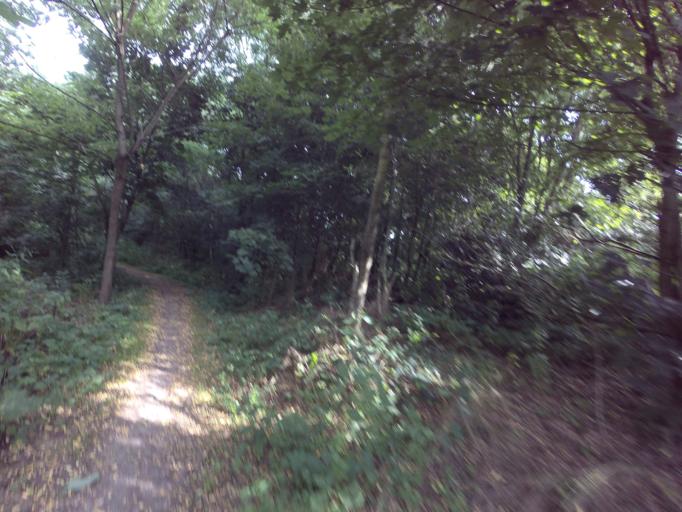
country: DE
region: North Rhine-Westphalia
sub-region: Regierungsbezirk Koln
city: Alsdorf
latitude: 50.8677
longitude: 6.1344
